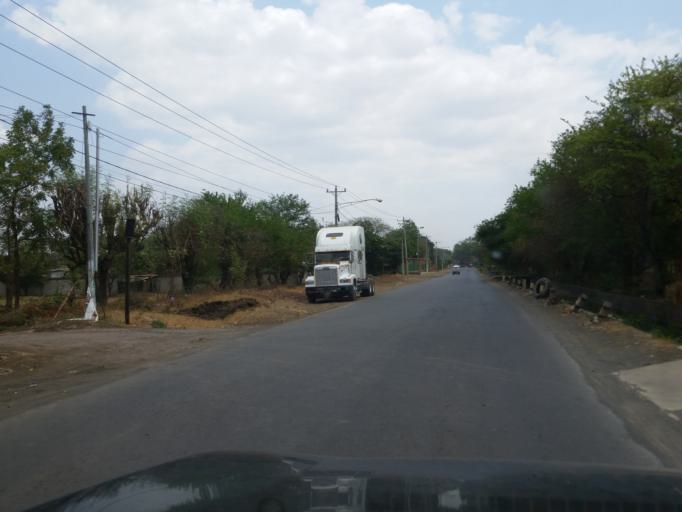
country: NI
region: Managua
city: Managua
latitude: 12.1249
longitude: -86.1788
